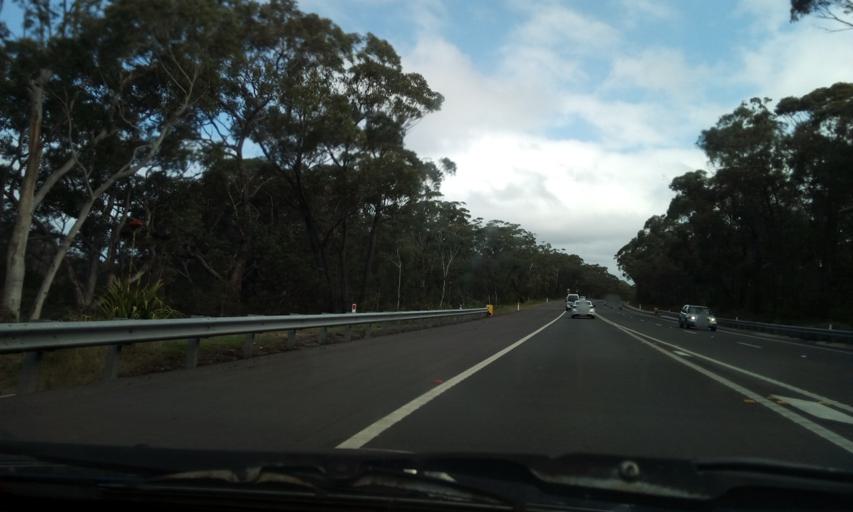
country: AU
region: New South Wales
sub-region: Wollongong
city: Bulli
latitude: -34.2704
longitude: 150.8960
